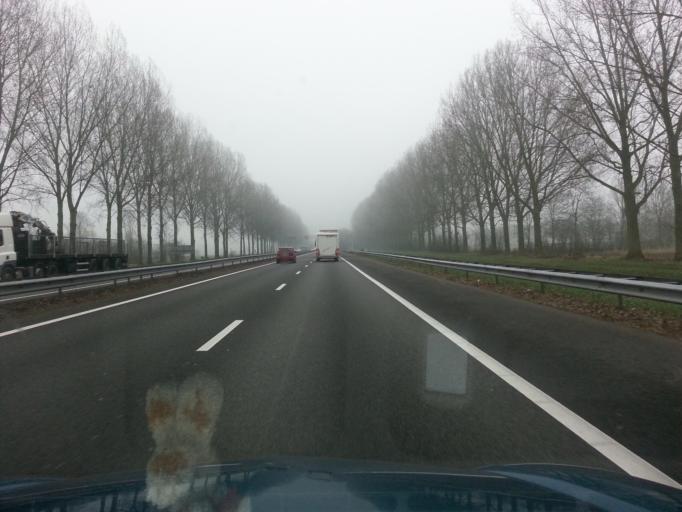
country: NL
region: Gelderland
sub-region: Gemeente Zevenaar
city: Zevenaar
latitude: 51.9335
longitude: 6.1003
